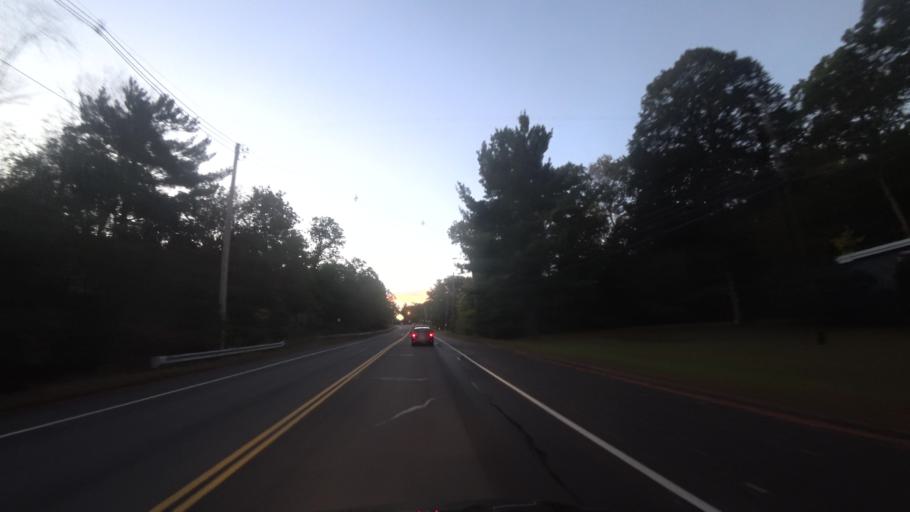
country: US
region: Massachusetts
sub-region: Middlesex County
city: Wakefield
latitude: 42.4895
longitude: -71.0484
